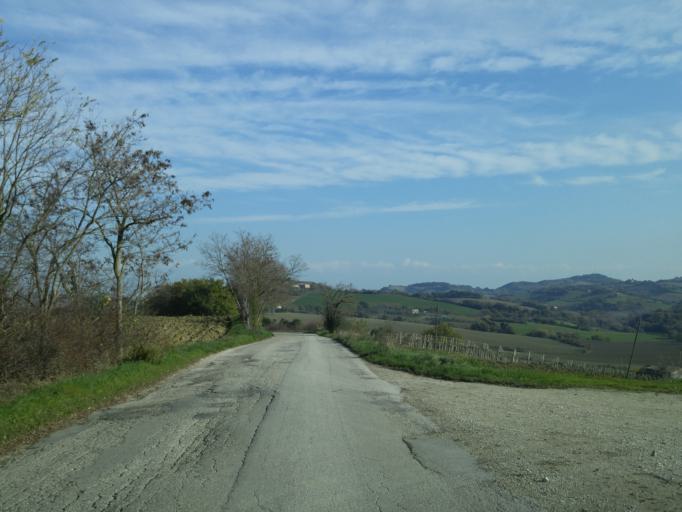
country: IT
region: The Marches
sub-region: Provincia di Pesaro e Urbino
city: Lucrezia
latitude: 43.8158
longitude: 12.9115
